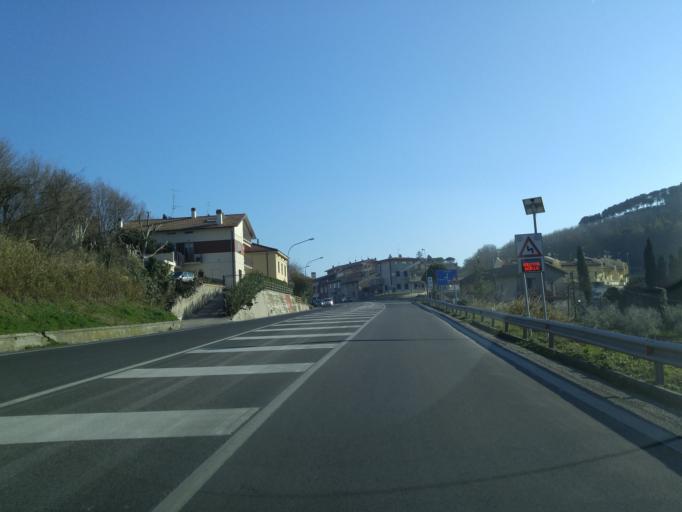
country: IT
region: The Marches
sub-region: Provincia di Pesaro e Urbino
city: Gradara
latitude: 43.9442
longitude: 12.8209
